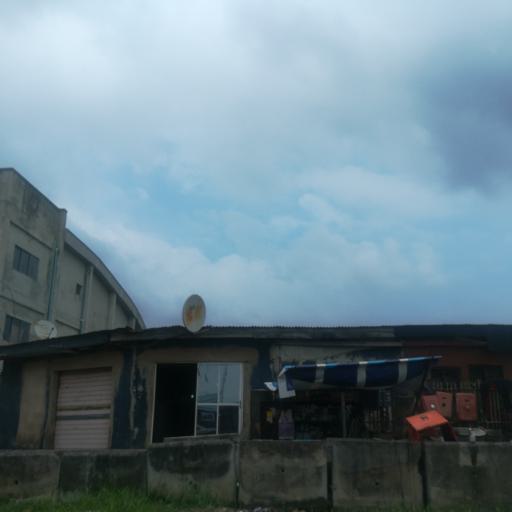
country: NG
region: Lagos
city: Ojota
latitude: 6.5857
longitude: 3.3885
